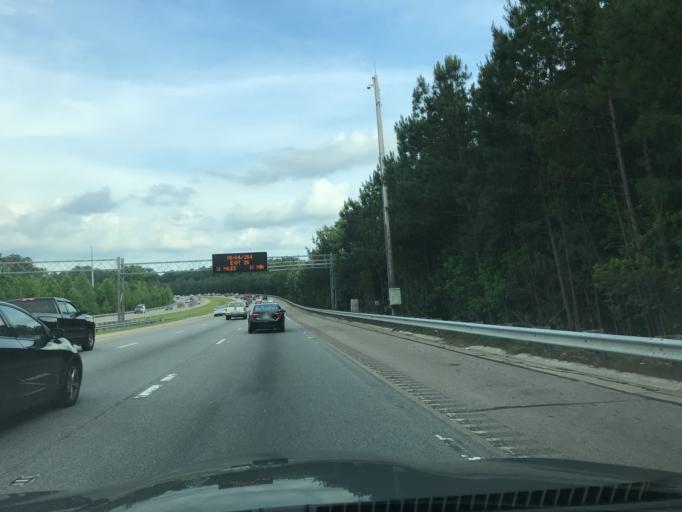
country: US
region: North Carolina
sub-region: Wake County
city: West Raleigh
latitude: 35.9027
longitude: -78.6330
